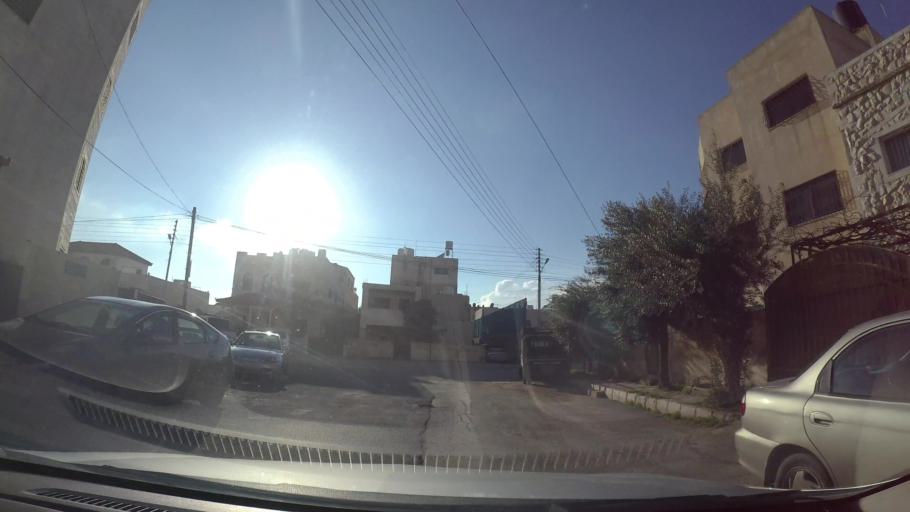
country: JO
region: Amman
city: Al Bunayyat ash Shamaliyah
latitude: 31.8978
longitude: 35.9126
